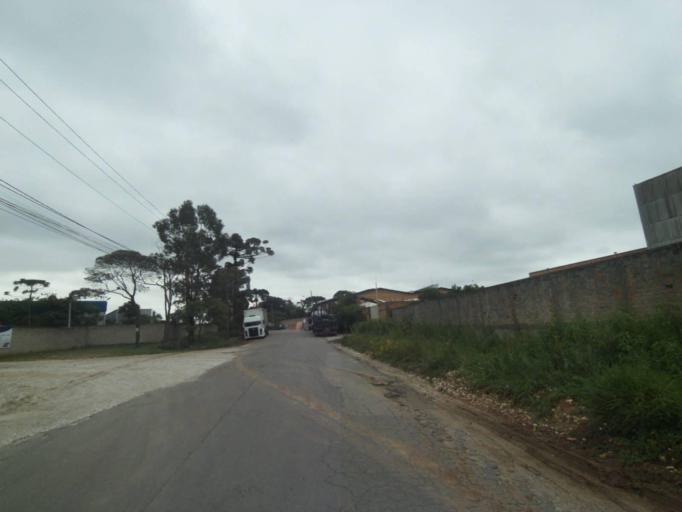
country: BR
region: Parana
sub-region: Curitiba
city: Curitiba
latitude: -25.5213
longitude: -49.3274
